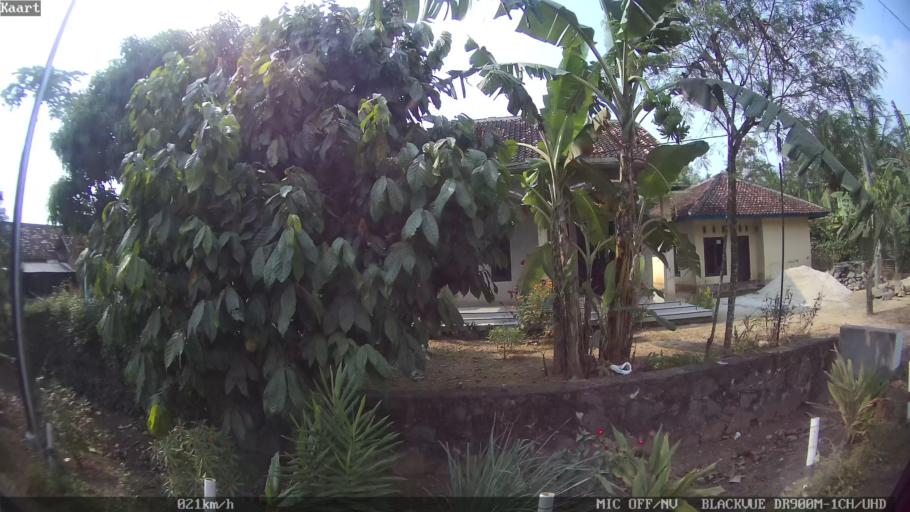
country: ID
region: Lampung
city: Kedondong
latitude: -5.4106
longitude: 105.0124
